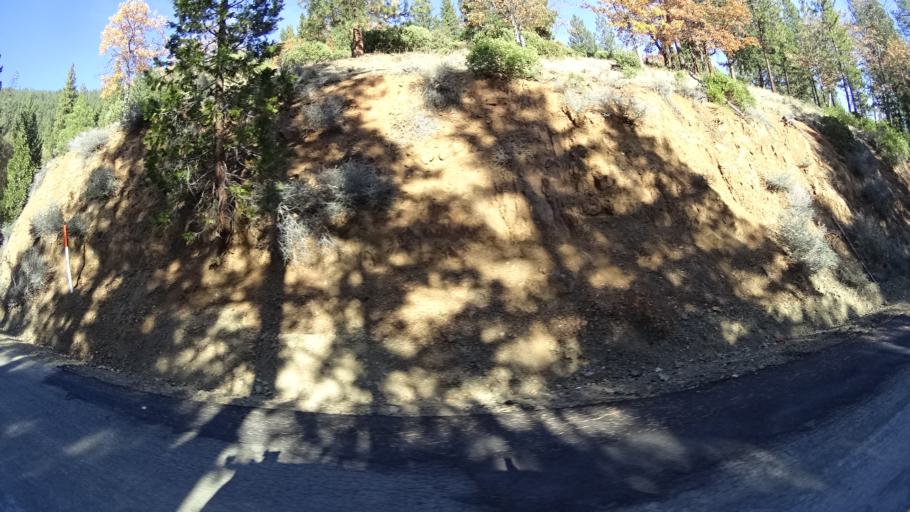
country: US
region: California
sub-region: Siskiyou County
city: Yreka
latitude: 41.7302
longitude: -122.7226
